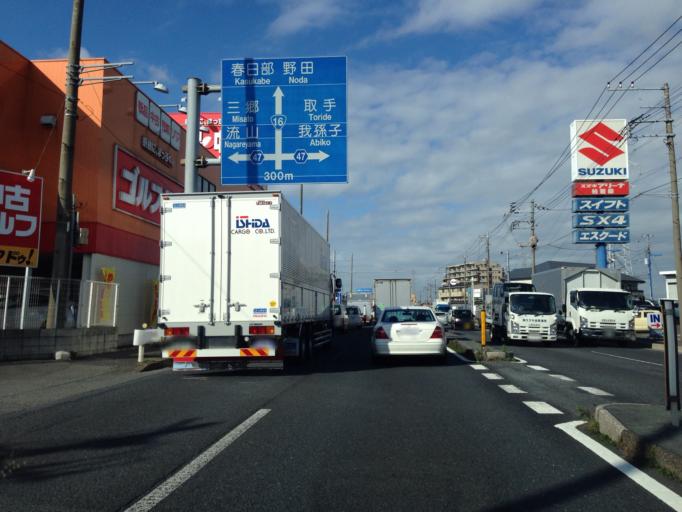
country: JP
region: Chiba
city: Kashiwa
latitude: 35.8889
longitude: 139.9614
